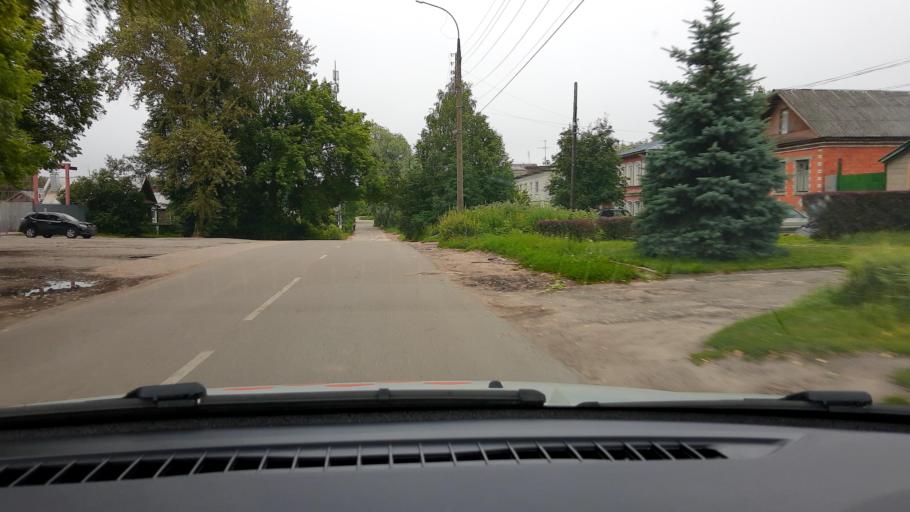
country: RU
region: Nizjnij Novgorod
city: Bogorodsk
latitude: 56.0956
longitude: 43.5111
